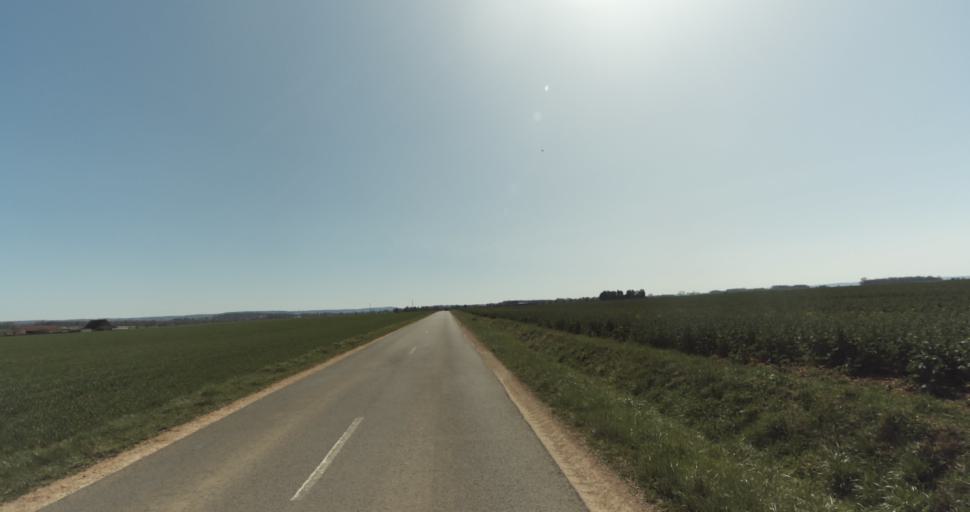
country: FR
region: Lower Normandy
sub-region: Departement du Calvados
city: Saint-Pierre-sur-Dives
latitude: 49.0058
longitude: -0.0251
